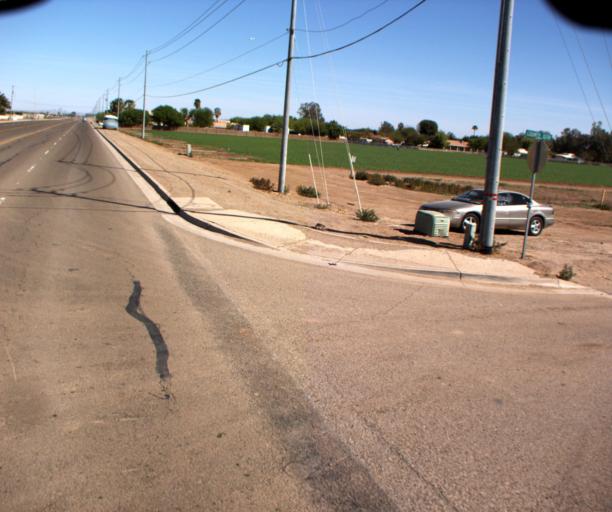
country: US
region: Arizona
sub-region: Yuma County
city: Somerton
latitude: 32.6402
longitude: -114.6500
